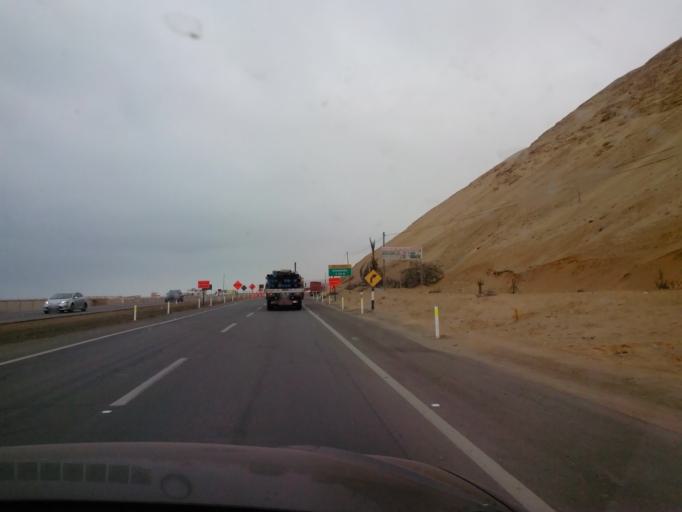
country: PE
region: Ica
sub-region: Provincia de Chincha
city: San Pedro
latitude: -13.3274
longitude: -76.2406
